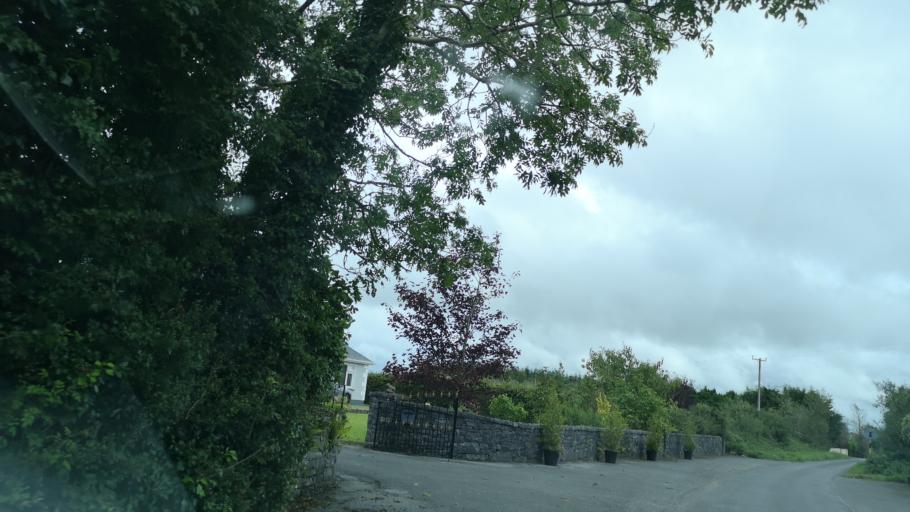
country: IE
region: Connaught
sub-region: County Galway
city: Loughrea
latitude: 53.2988
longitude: -8.5958
